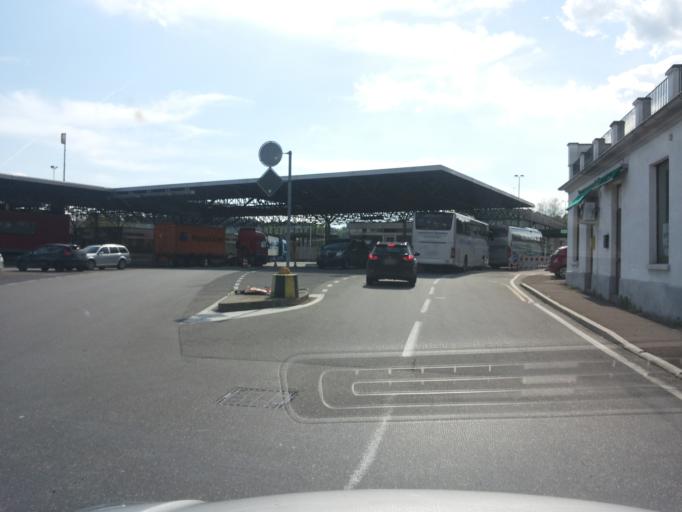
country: IT
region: Lombardy
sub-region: Provincia di Varese
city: Baraggia
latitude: 45.8414
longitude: 8.9147
